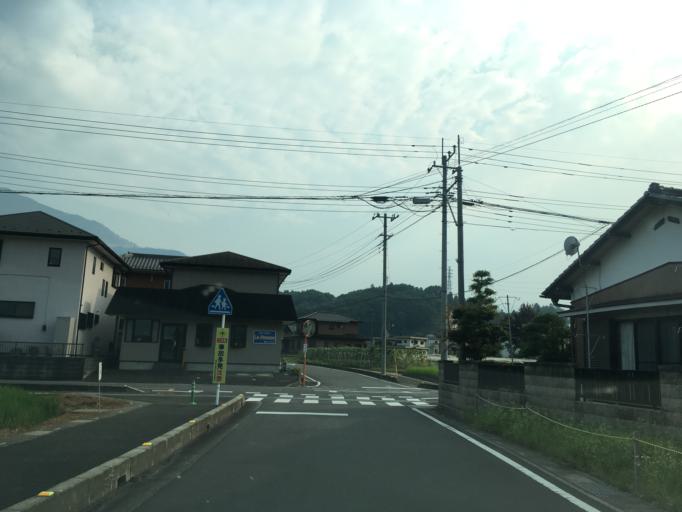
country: JP
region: Saitama
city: Chichibu
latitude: 35.9920
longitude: 139.0969
